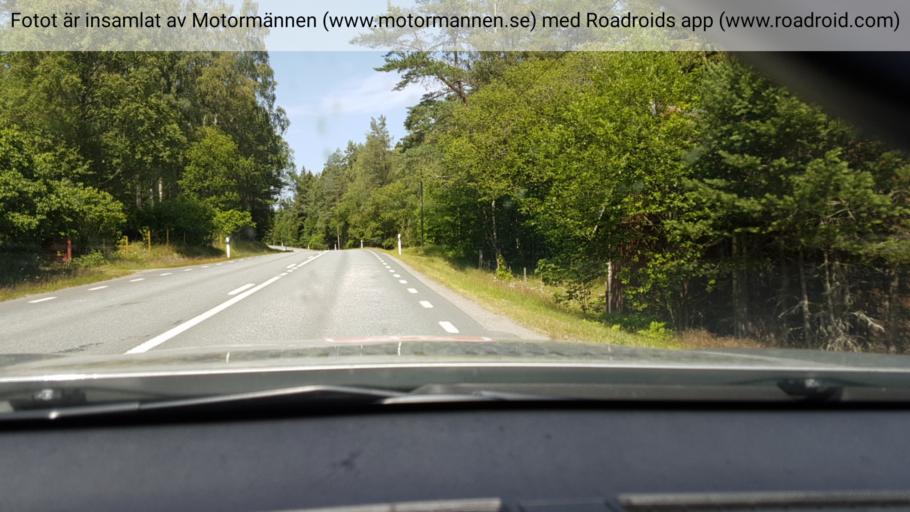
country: SE
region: Joenkoeping
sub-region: Nassjo Kommun
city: Bodafors
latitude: 57.5384
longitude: 14.7889
